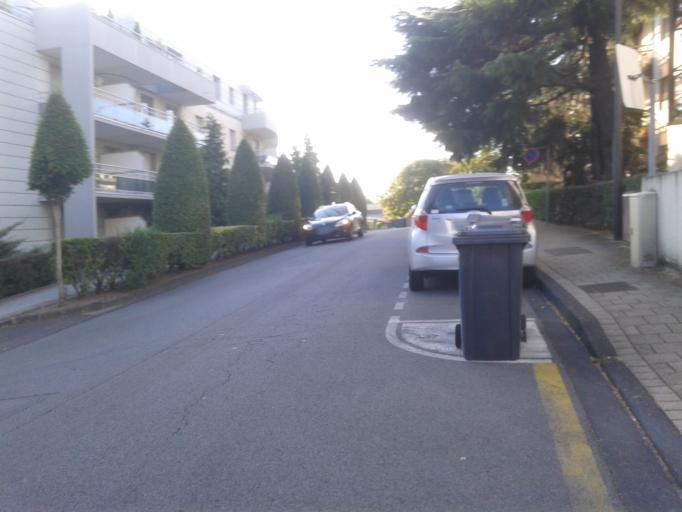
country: FR
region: Auvergne
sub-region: Departement du Puy-de-Dome
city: Chamalieres
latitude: 45.7718
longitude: 3.0678
